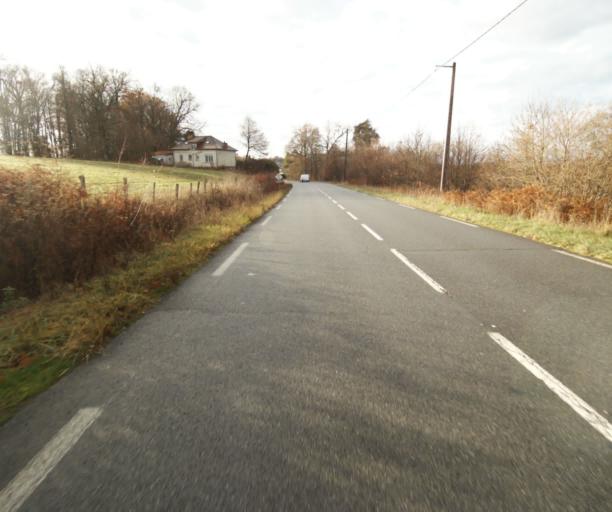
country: FR
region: Limousin
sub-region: Departement de la Correze
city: Saint-Mexant
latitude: 45.2617
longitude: 1.6362
